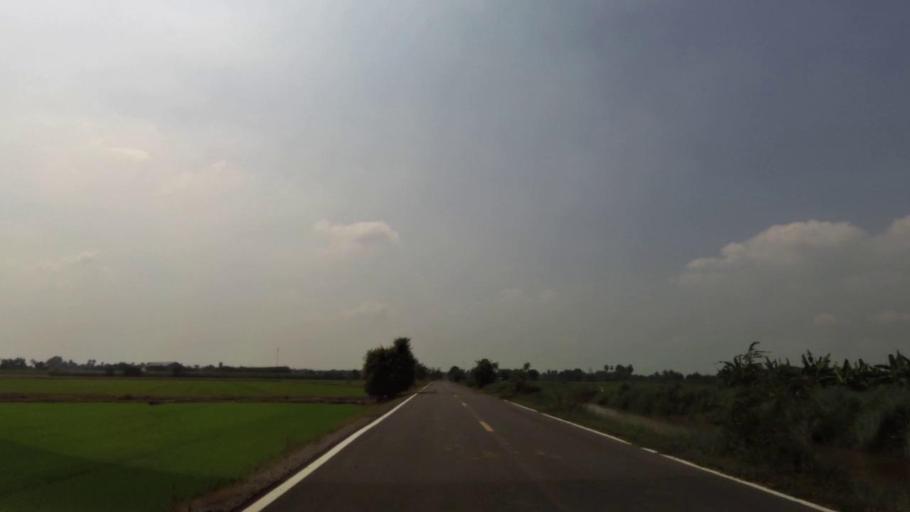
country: TH
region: Ang Thong
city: Pho Thong
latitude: 14.6156
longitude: 100.4001
